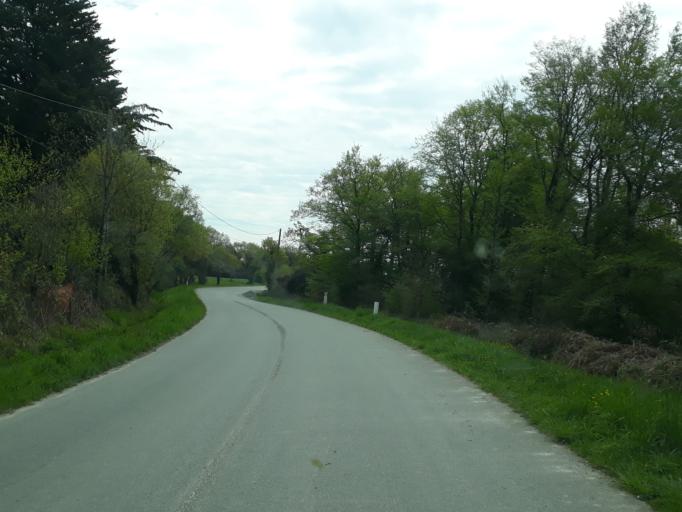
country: FR
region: Pays de la Loire
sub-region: Departement de la Loire-Atlantique
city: Saint-Molf
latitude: 47.3653
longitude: -2.4128
